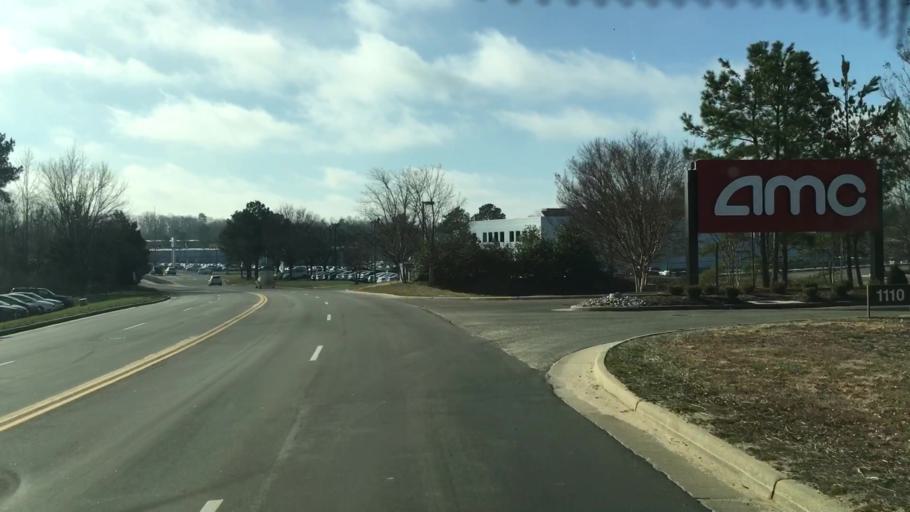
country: US
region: Virginia
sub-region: Chesterfield County
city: Bon Air
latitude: 37.5067
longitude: -77.6179
